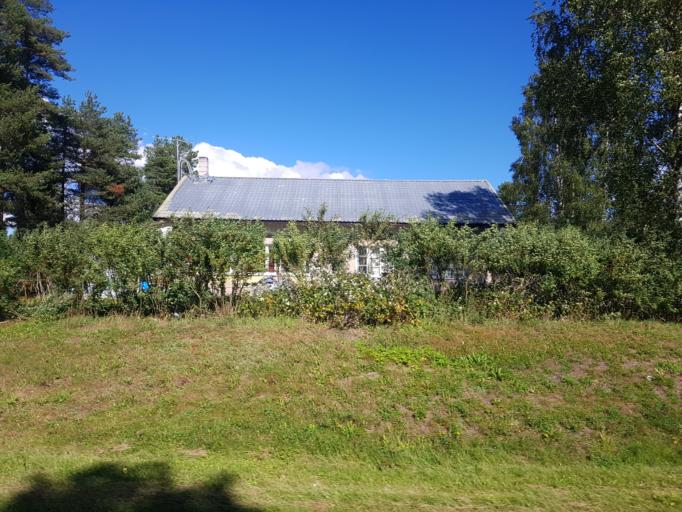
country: FI
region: Kainuu
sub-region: Kajaani
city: Sotkamo
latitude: 64.1331
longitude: 28.3527
